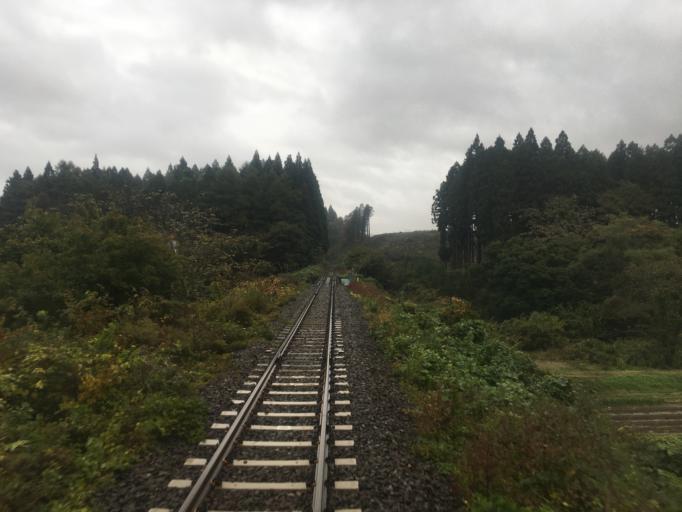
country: JP
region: Yamagata
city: Shinjo
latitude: 38.7648
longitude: 140.4599
